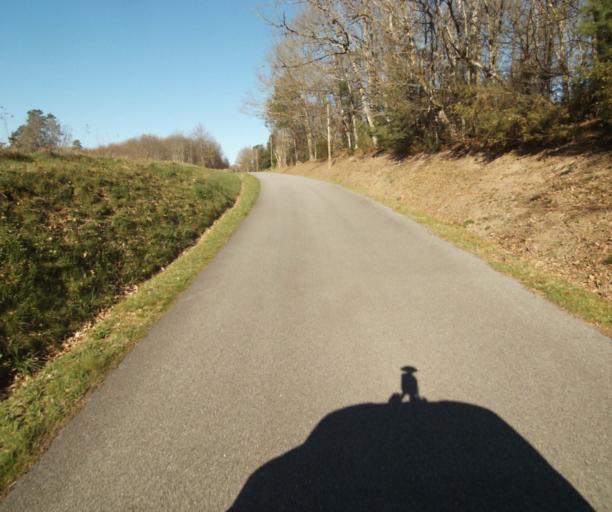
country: FR
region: Limousin
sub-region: Departement de la Correze
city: Correze
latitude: 45.2708
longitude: 1.9029
